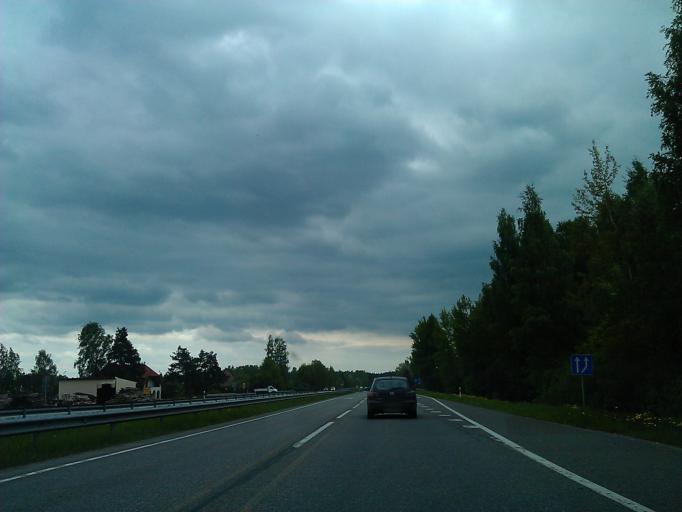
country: LV
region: Marupe
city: Marupe
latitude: 56.8590
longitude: 24.0640
